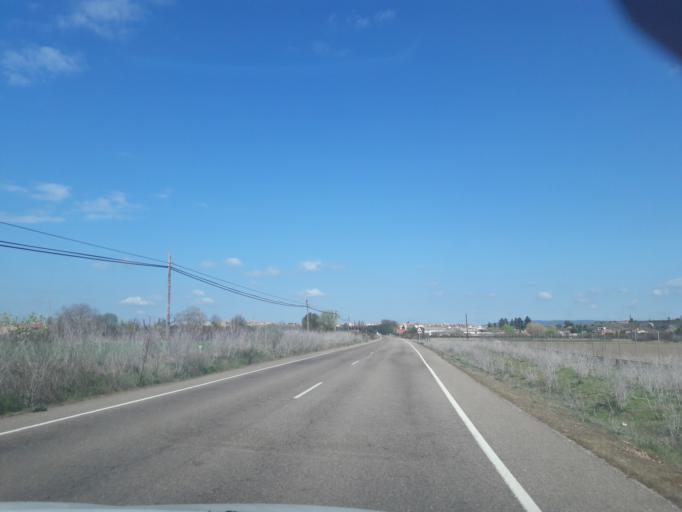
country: ES
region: Castille and Leon
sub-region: Provincia de Salamanca
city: Ciudad Rodrigo
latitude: 40.5837
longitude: -6.5081
